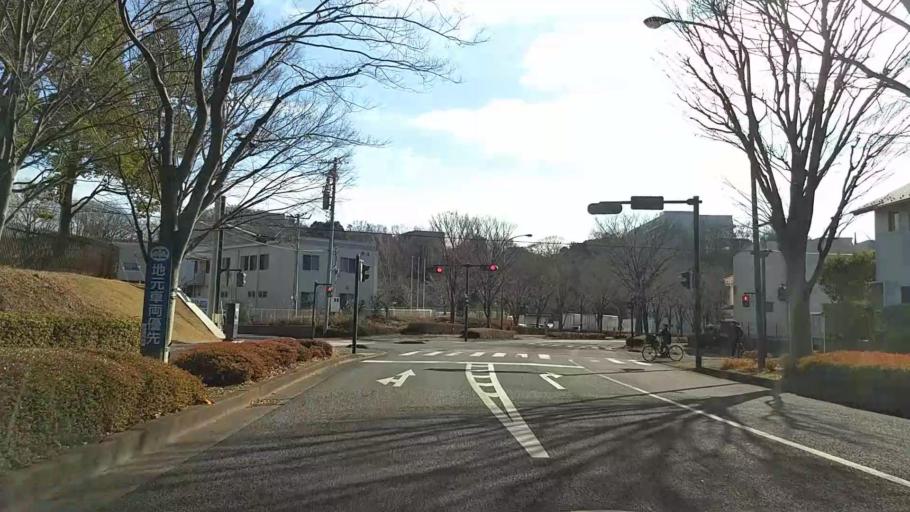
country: JP
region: Kanagawa
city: Atsugi
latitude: 35.4497
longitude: 139.3100
